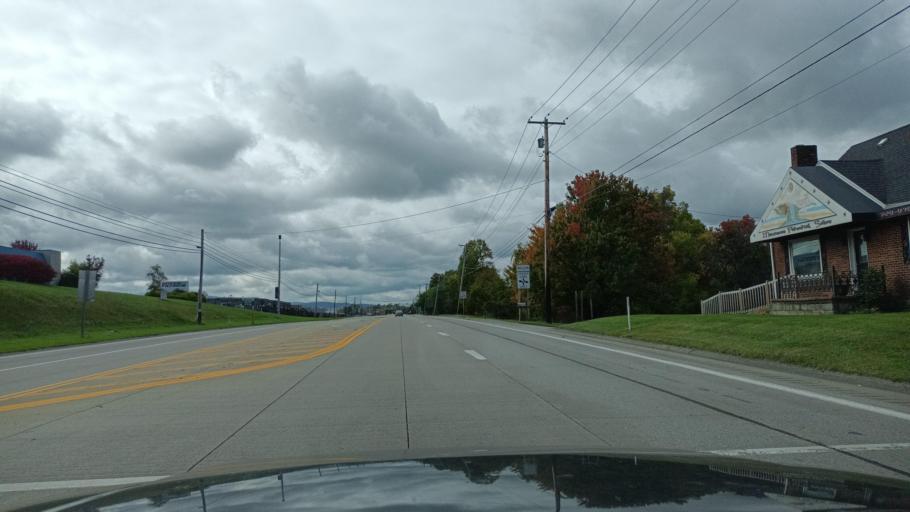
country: US
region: Pennsylvania
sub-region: Fayette County
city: Dunbar
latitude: 39.9499
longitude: -79.6542
